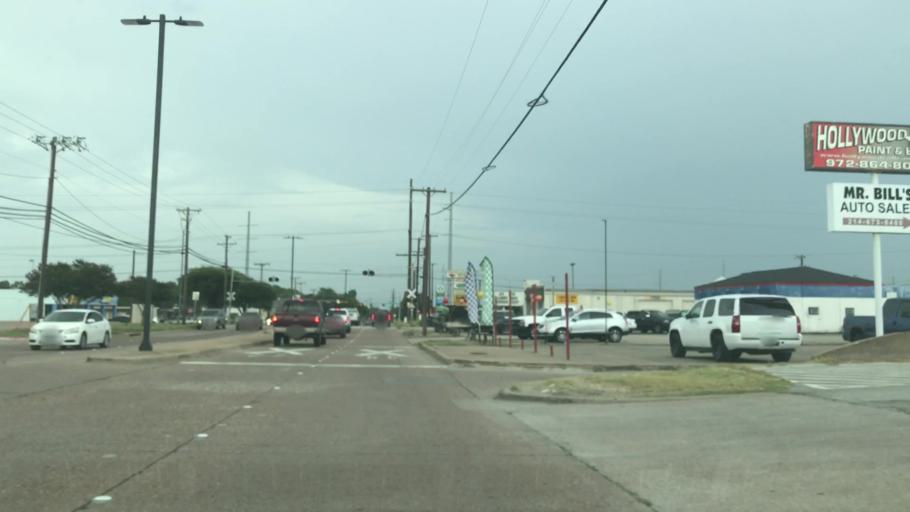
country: US
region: Texas
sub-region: Dallas County
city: Garland
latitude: 32.8788
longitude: -96.6679
